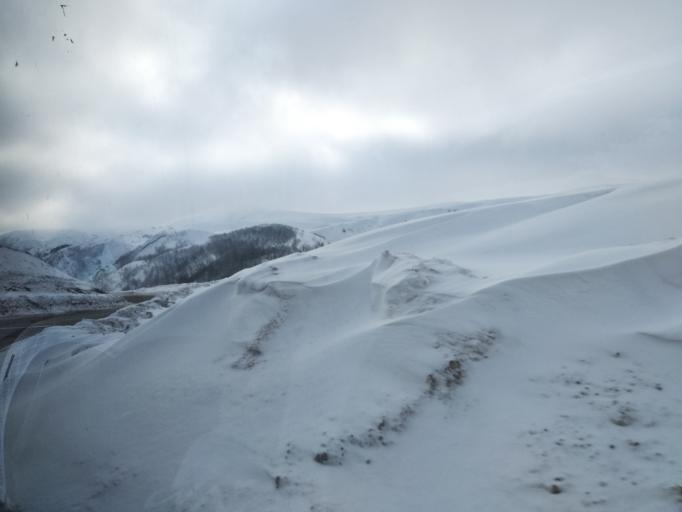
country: TR
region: Erzincan
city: Catalarmut
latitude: 39.8944
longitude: 39.3726
